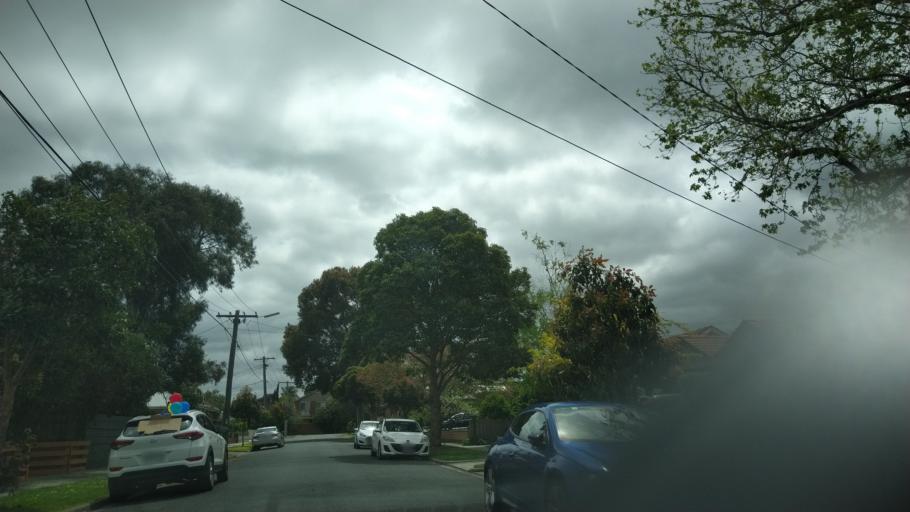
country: AU
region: Victoria
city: Murrumbeena
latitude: -37.8951
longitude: 145.0620
